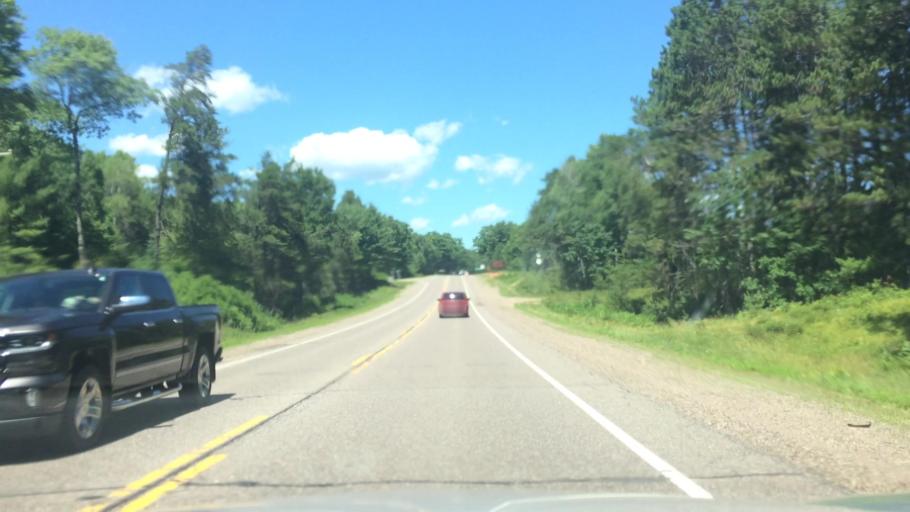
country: US
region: Wisconsin
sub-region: Vilas County
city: Lac du Flambeau
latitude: 45.7766
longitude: -89.7153
